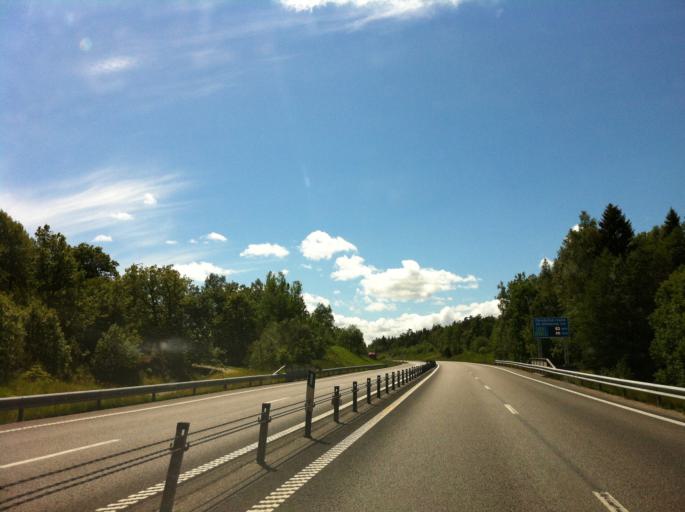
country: SE
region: Vaestra Goetaland
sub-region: Vanersborgs Kommun
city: Vanersborg
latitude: 58.3687
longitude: 12.2728
